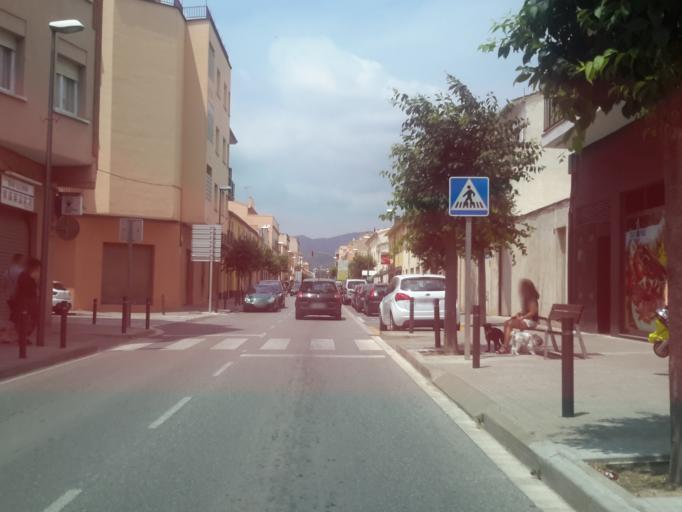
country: ES
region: Catalonia
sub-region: Provincia de Barcelona
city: Sant Marti Sarroca
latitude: 41.3857
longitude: 1.6133
